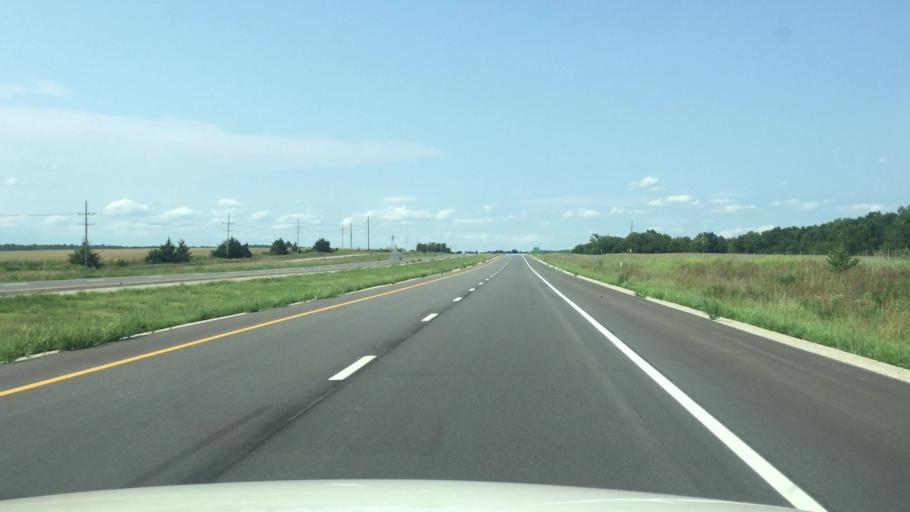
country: US
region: Kansas
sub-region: Linn County
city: La Cygne
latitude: 38.3192
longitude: -94.6774
